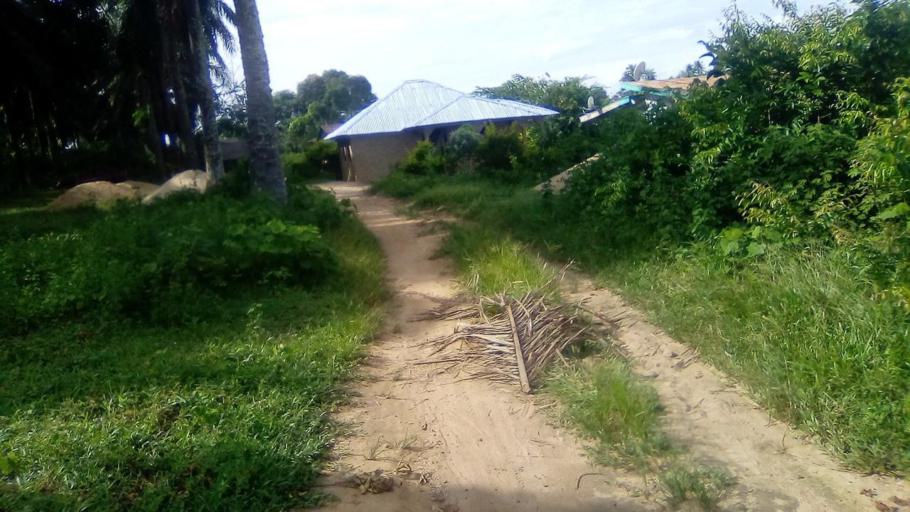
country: SL
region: Southern Province
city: Pujehun
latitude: 7.3632
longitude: -11.7215
